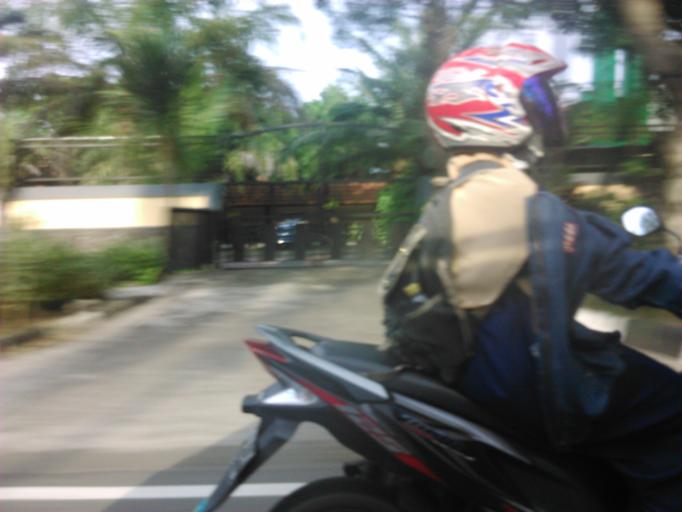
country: ID
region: East Java
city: Semampir
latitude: -7.2878
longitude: 112.7808
